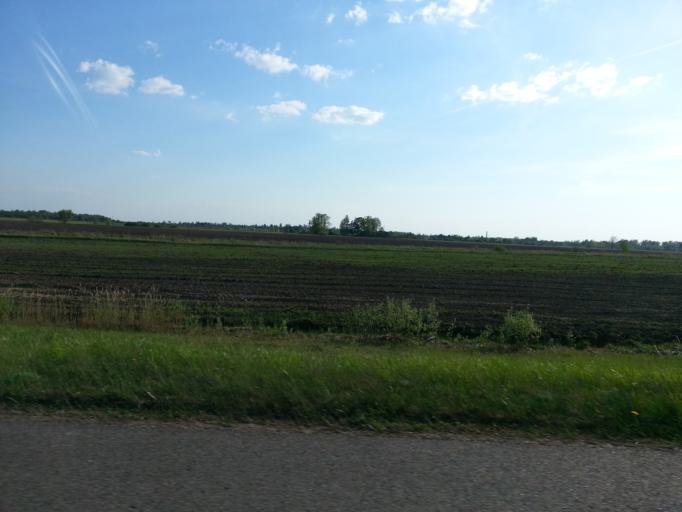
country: LT
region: Panevezys
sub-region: Panevezys City
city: Panevezys
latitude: 55.6073
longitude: 24.4319
